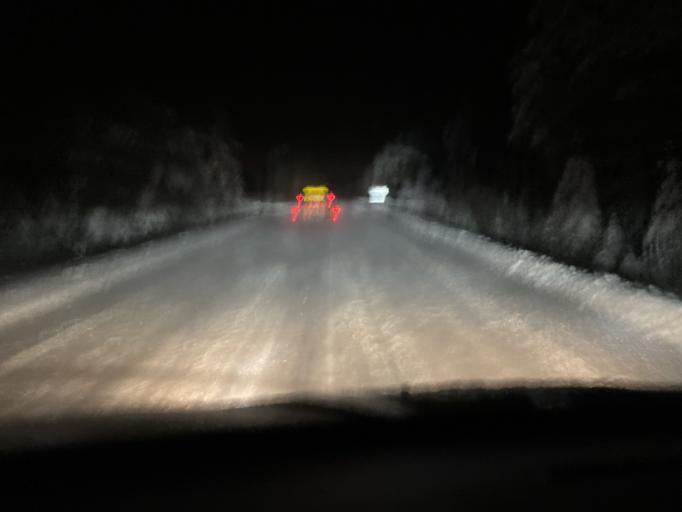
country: EE
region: Harju
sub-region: Kuusalu vald
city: Kuusalu
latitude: 59.4242
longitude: 25.3846
